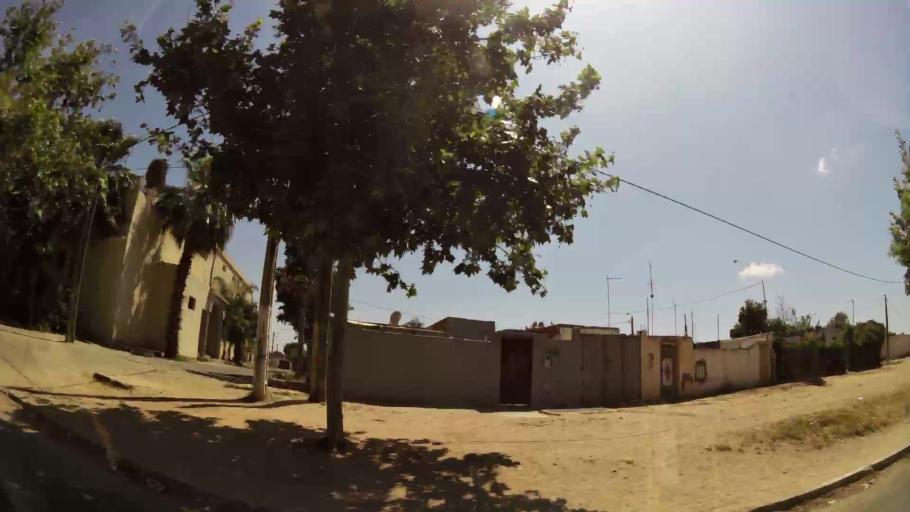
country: MA
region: Gharb-Chrarda-Beni Hssen
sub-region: Kenitra Province
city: Kenitra
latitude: 34.2320
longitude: -6.5347
